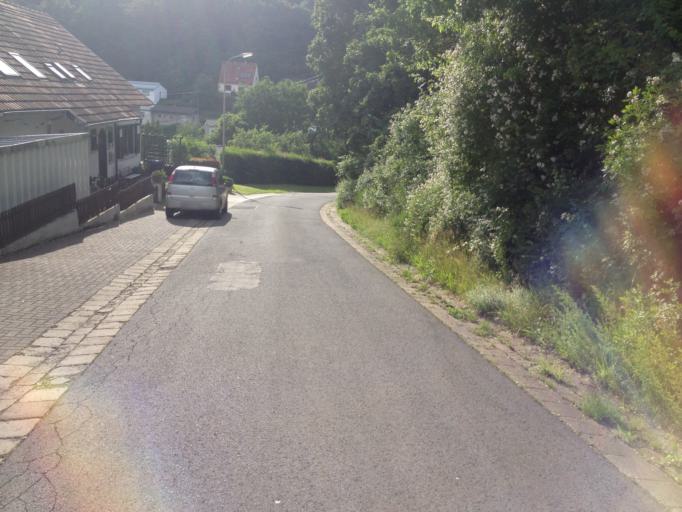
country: DE
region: Rheinland-Pfalz
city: Breitenbach
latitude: 49.4624
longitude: 7.2423
